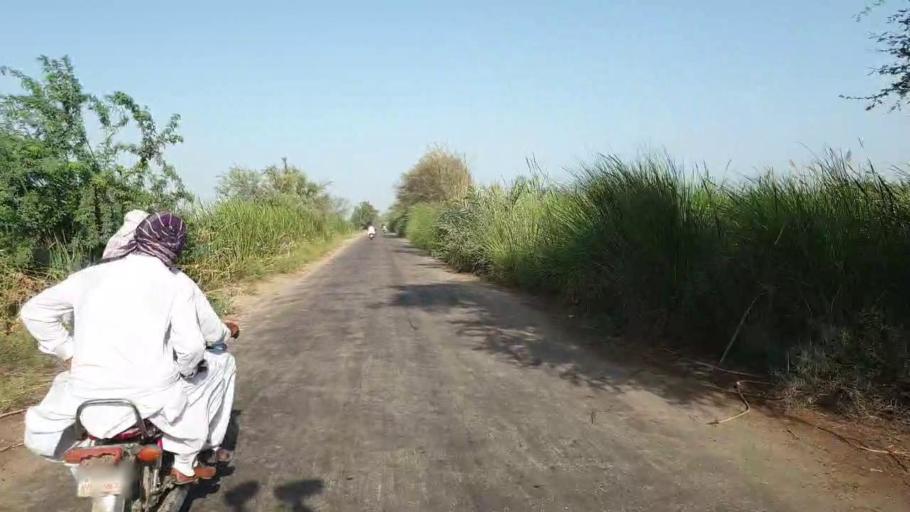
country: PK
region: Sindh
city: Nawabshah
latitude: 26.3750
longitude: 68.4656
